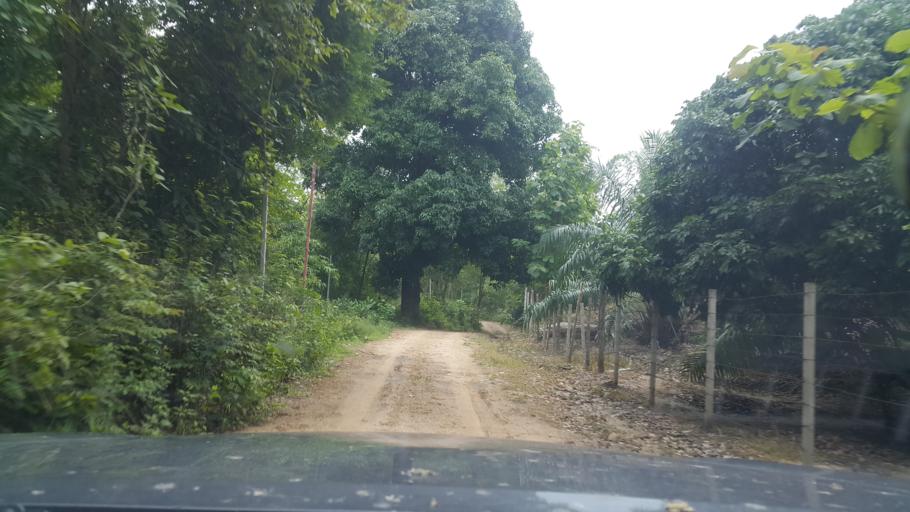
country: TH
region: Chiang Mai
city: Hang Dong
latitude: 18.6973
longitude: 98.8611
